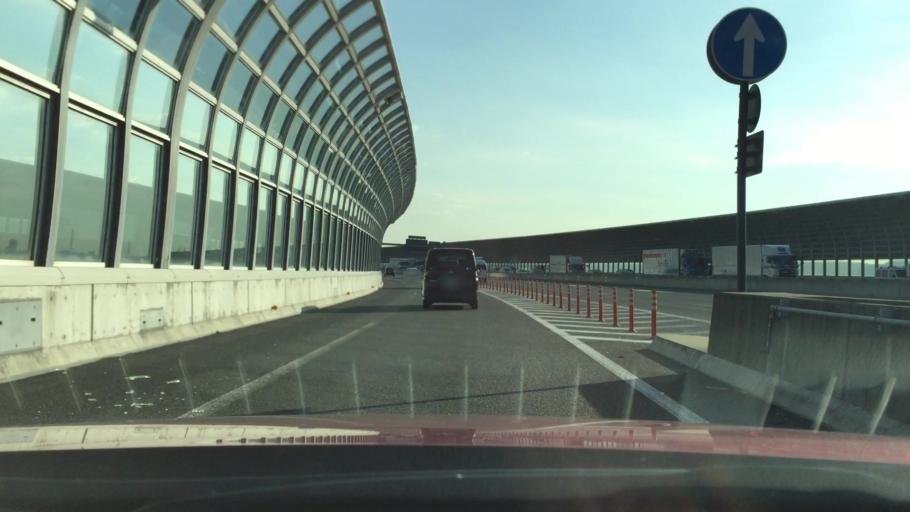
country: JP
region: Osaka
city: Daitocho
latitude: 34.7202
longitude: 135.5978
